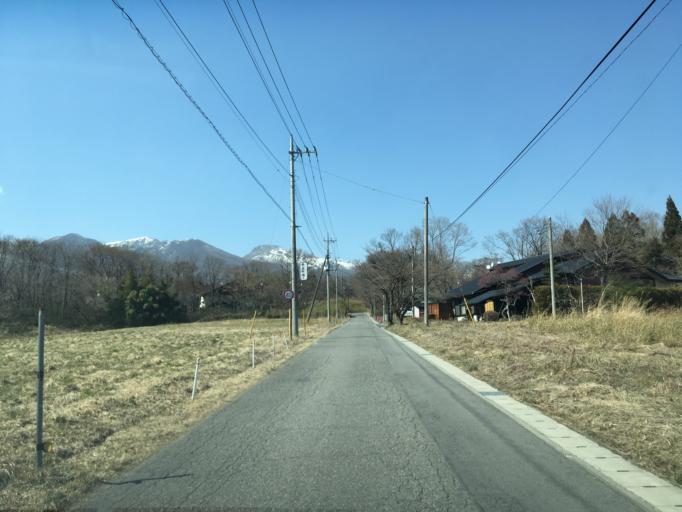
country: JP
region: Tochigi
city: Kuroiso
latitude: 37.0669
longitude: 140.0039
